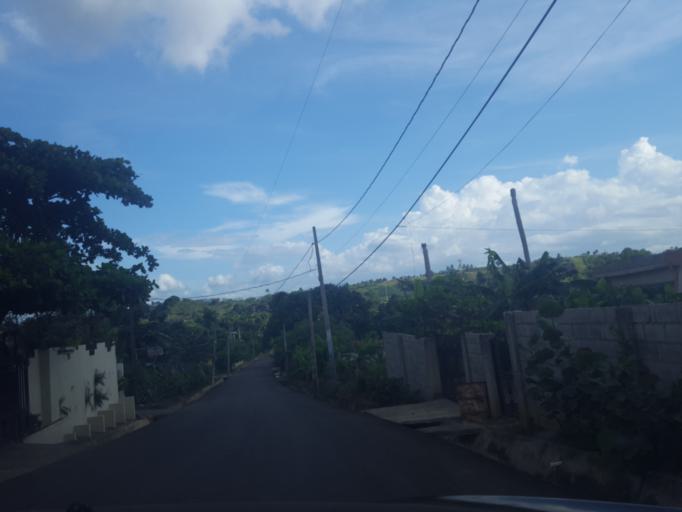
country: DO
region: Santiago
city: Licey al Medio
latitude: 19.3635
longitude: -70.6326
